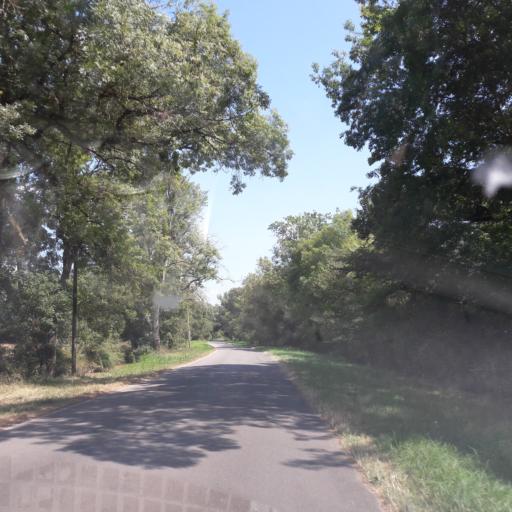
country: FR
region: Aquitaine
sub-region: Departement de la Gironde
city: Cadaujac
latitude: 44.7366
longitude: -0.5188
